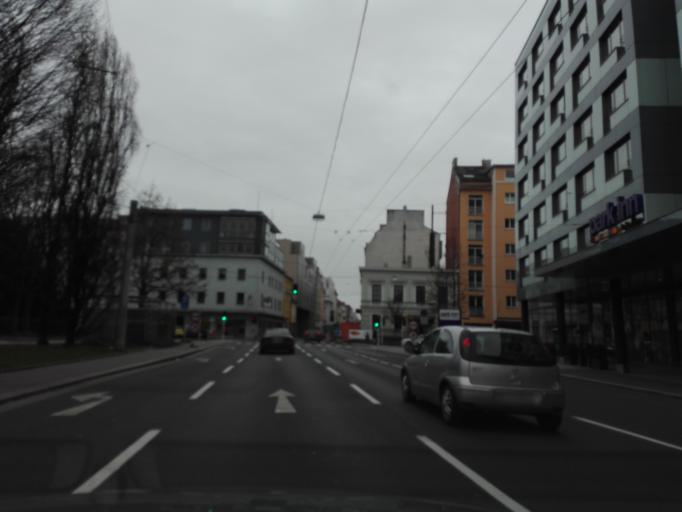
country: AT
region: Upper Austria
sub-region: Linz Stadt
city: Linz
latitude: 48.3010
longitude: 14.2932
